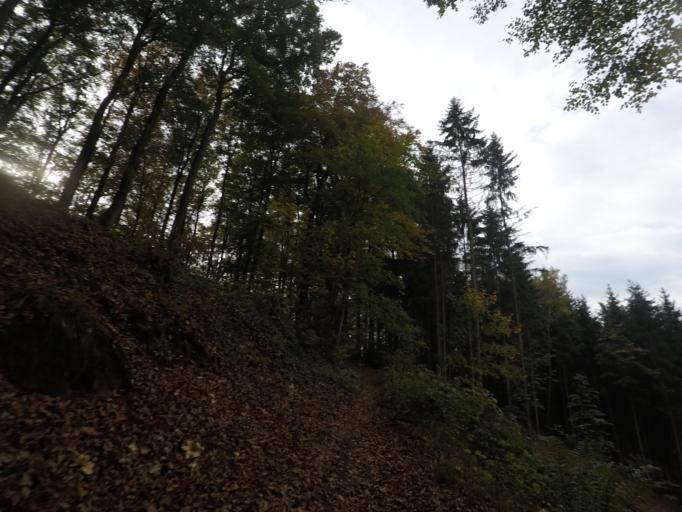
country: LU
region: Luxembourg
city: Itzig
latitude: 49.6046
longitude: 6.1891
